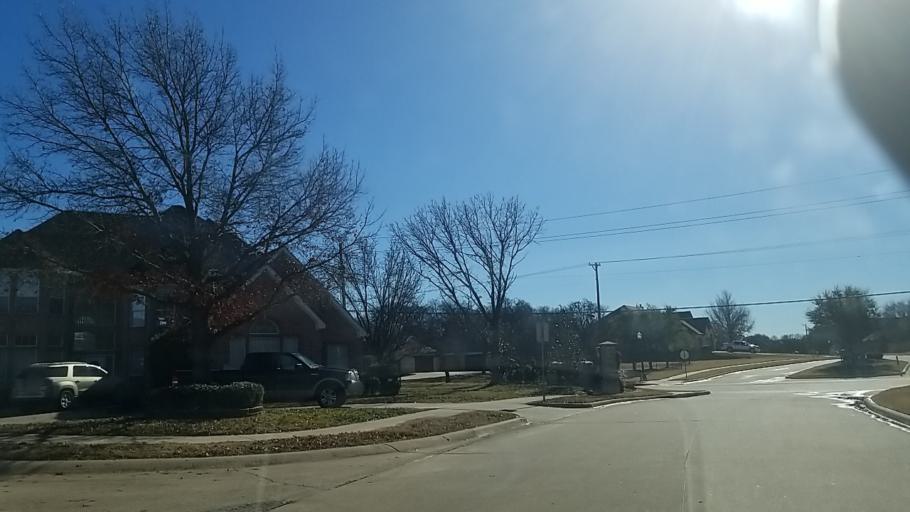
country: US
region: Texas
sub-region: Denton County
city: Corinth
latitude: 33.1555
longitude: -97.0809
